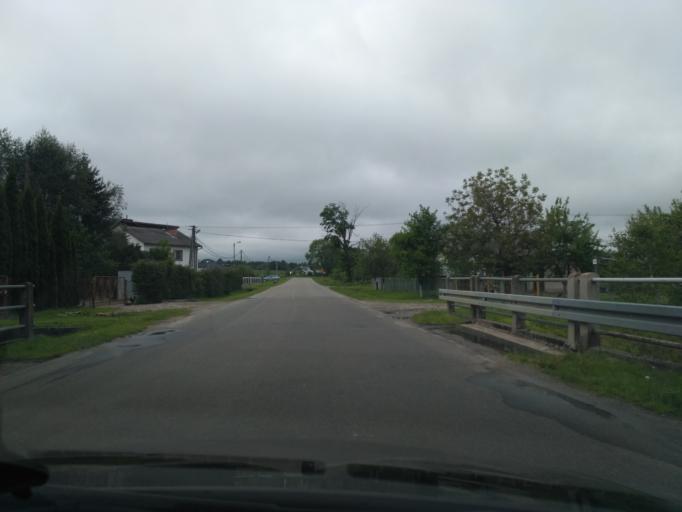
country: PL
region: Subcarpathian Voivodeship
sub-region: Powiat jasielski
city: Brzyska
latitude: 49.8216
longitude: 21.3960
